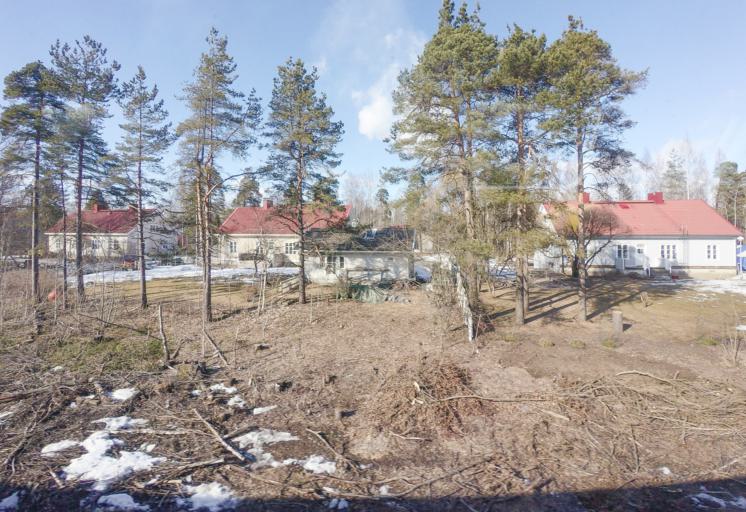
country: FI
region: South Karelia
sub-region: Lappeenranta
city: Lappeenranta
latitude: 61.0593
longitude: 28.2384
